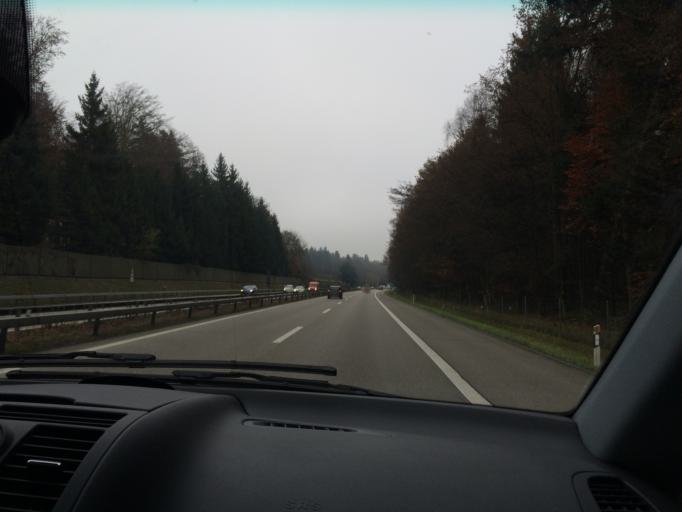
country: CH
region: Solothurn
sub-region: Bezirk Wasseramt
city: Kriegstetten
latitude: 47.1576
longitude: 7.5906
